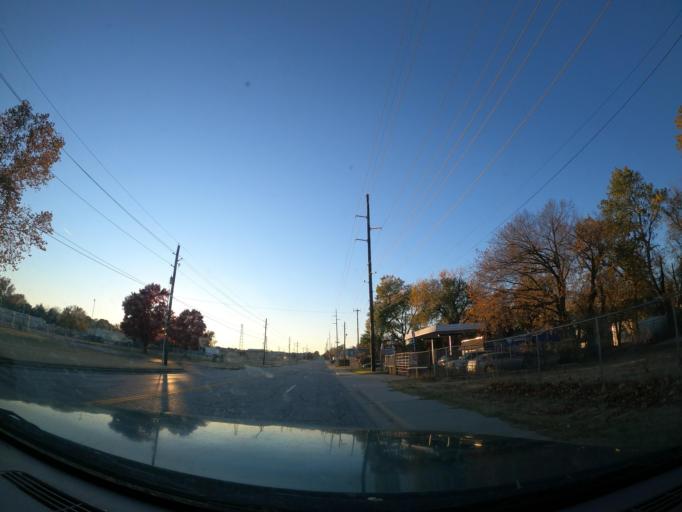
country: US
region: Oklahoma
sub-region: Tulsa County
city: Tulsa
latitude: 36.1407
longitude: -95.9126
